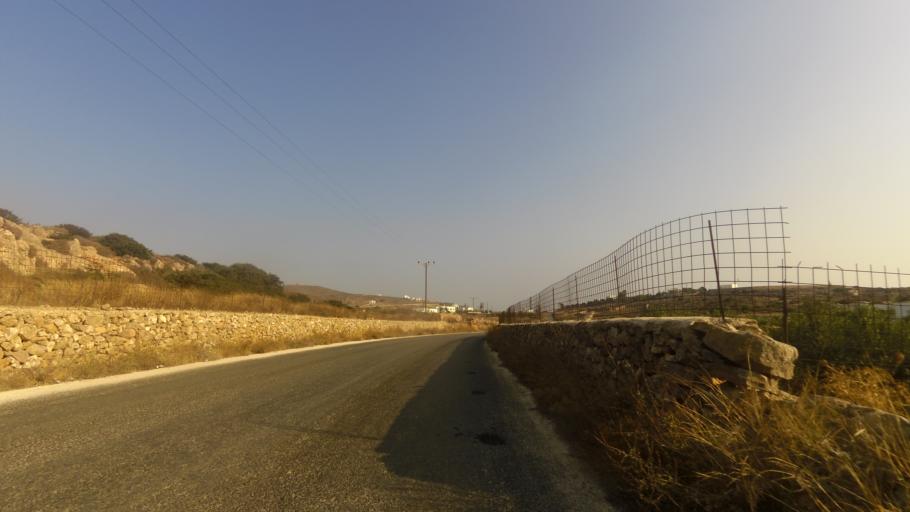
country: GR
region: South Aegean
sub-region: Nomos Kykladon
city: Antiparos
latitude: 37.0294
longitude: 25.0754
